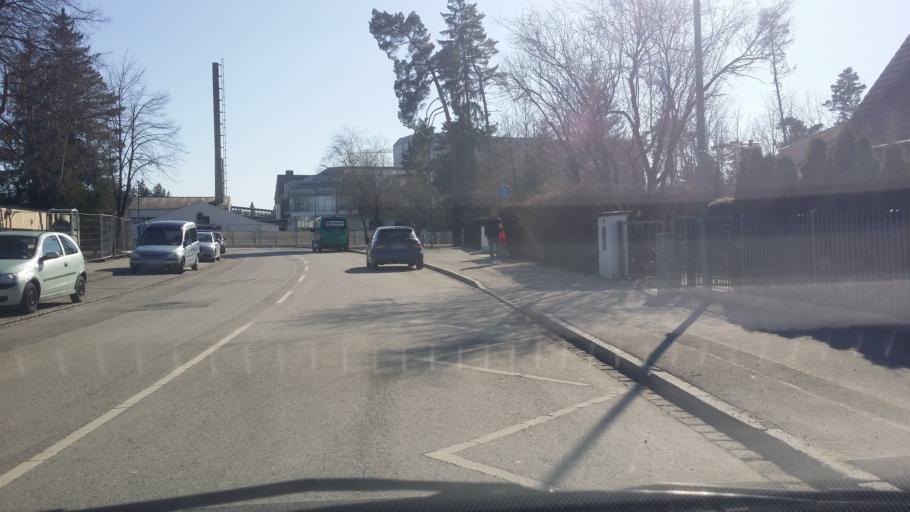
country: DE
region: Bavaria
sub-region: Upper Bavaria
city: Geretsried
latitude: 47.8826
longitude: 11.4728
